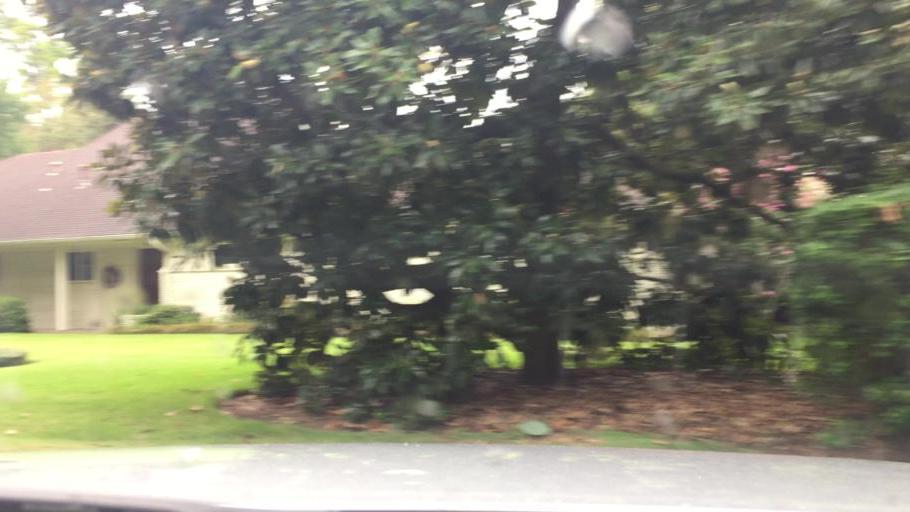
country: US
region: Texas
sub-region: Harris County
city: Hunters Creek Village
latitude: 29.7662
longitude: -95.5051
